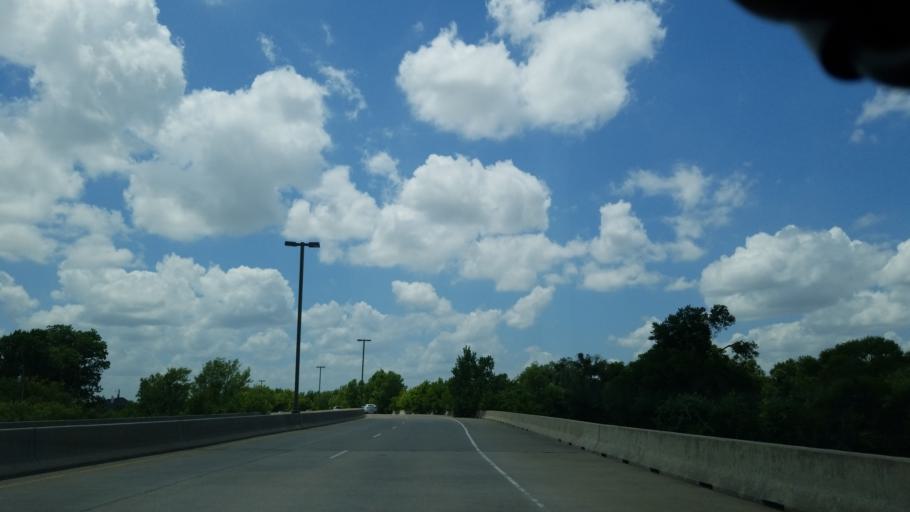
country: US
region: Texas
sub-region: Dallas County
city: Carrollton
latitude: 32.9659
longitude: -96.9420
